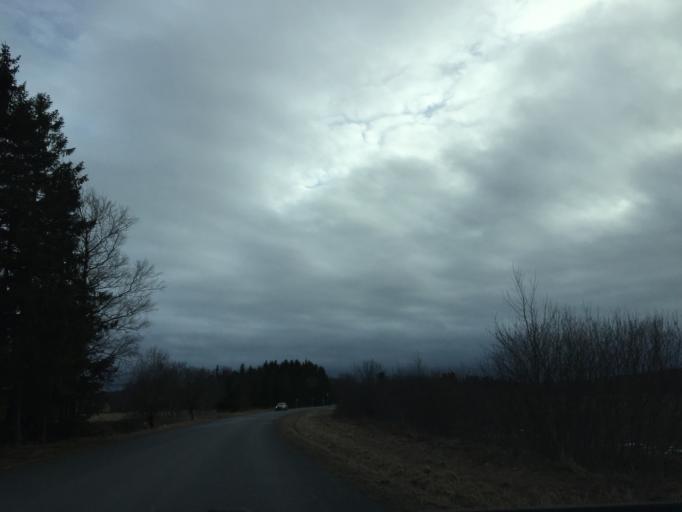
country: EE
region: Laeaene
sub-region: Ridala Parish
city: Uuemoisa
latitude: 58.8231
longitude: 23.5677
